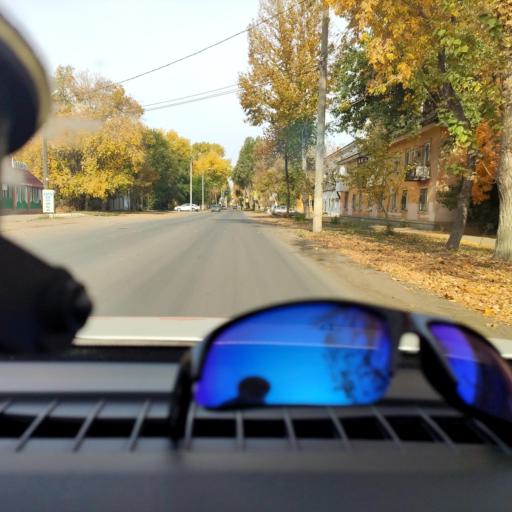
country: RU
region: Samara
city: Samara
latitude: 53.1117
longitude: 50.0751
